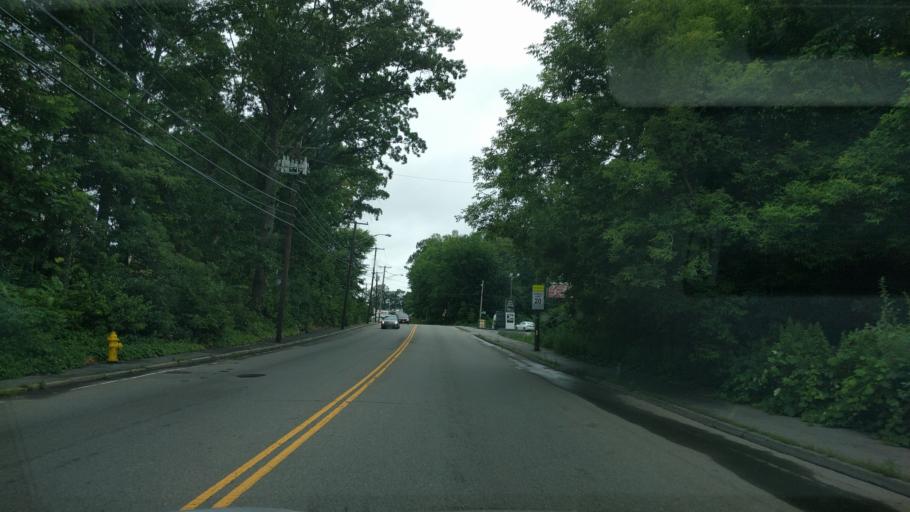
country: US
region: Massachusetts
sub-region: Worcester County
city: Sunderland
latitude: 42.2425
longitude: -71.7552
